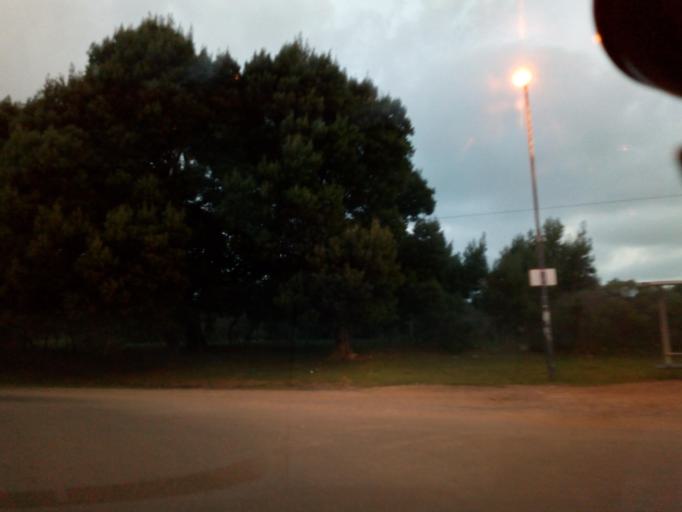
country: AR
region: Buenos Aires
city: Mar del Plata
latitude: -38.0800
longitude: -57.5847
